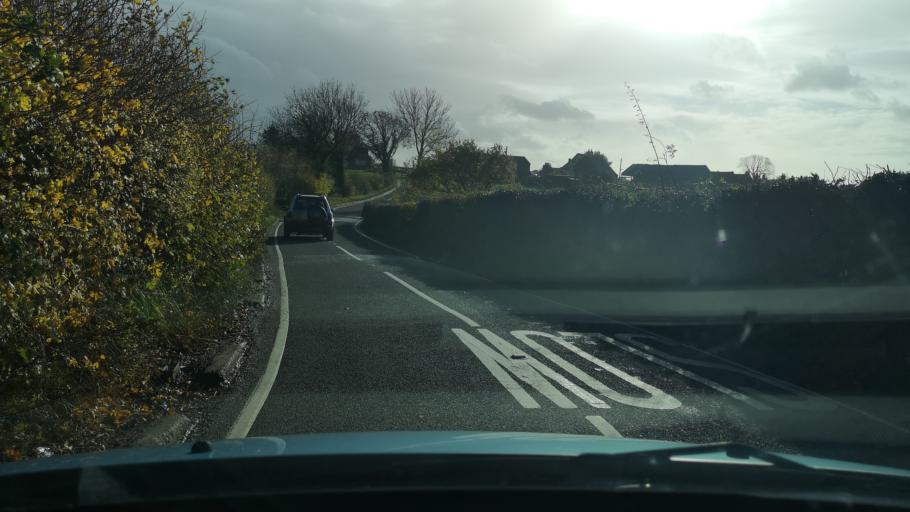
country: GB
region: England
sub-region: City and Borough of Wakefield
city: Ryhill
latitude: 53.6393
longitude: -1.4195
